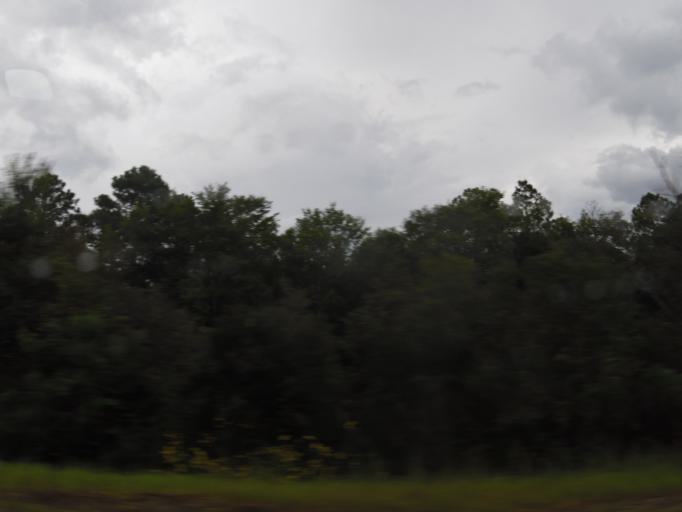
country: US
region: Georgia
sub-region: Wayne County
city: Jesup
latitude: 31.4494
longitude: -81.6965
